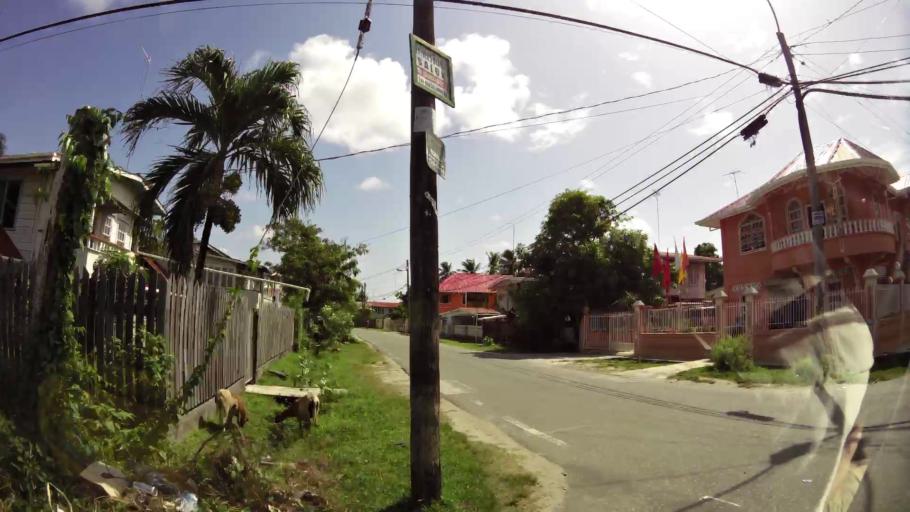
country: GY
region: Demerara-Mahaica
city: Mahaica Village
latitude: 6.7591
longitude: -57.9918
